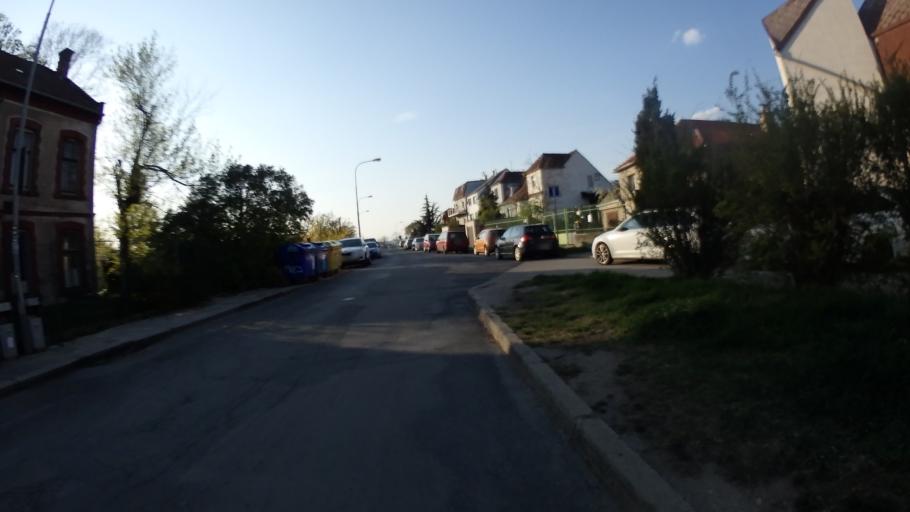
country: CZ
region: South Moravian
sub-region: Mesto Brno
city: Brno
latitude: 49.1820
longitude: 16.5882
